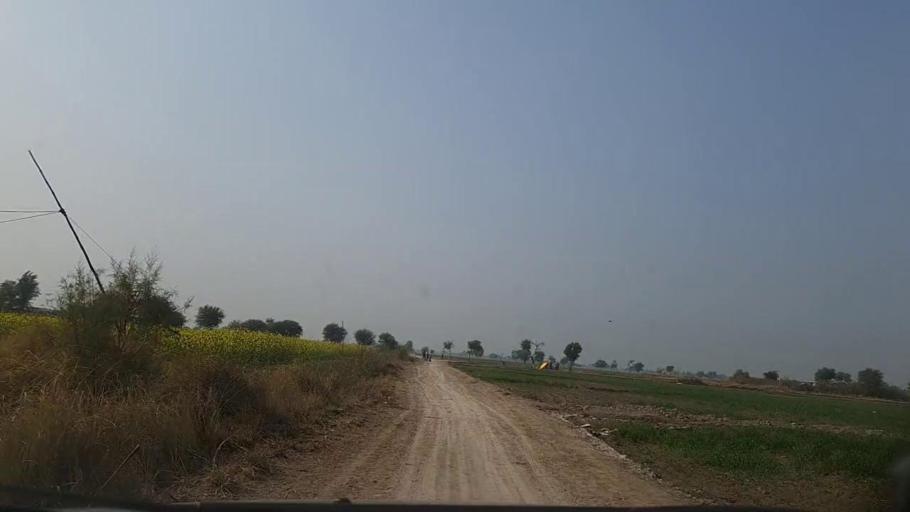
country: PK
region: Sindh
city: Sanghar
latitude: 26.0345
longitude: 68.9967
